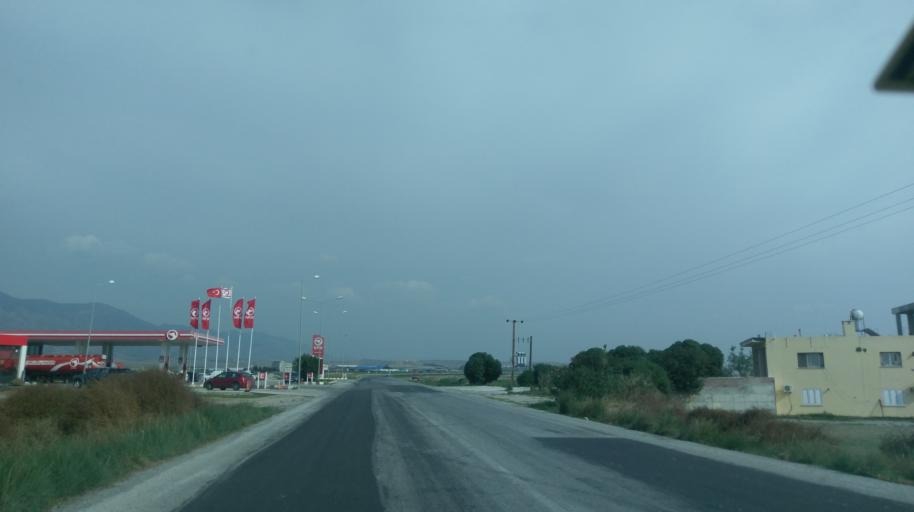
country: CY
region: Lefkosia
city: Geri
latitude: 35.2237
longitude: 33.5194
